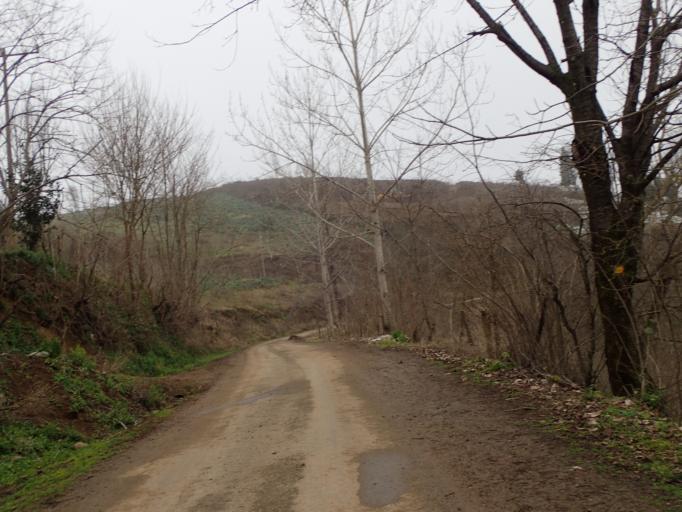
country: TR
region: Ordu
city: Camas
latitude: 40.9222
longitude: 37.5588
